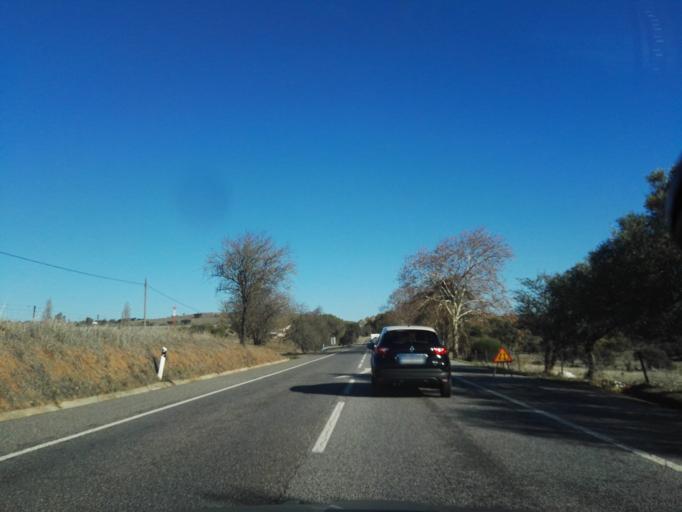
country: PT
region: Evora
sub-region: Vila Vicosa
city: Vila Vicosa
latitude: 38.8478
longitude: -7.3549
